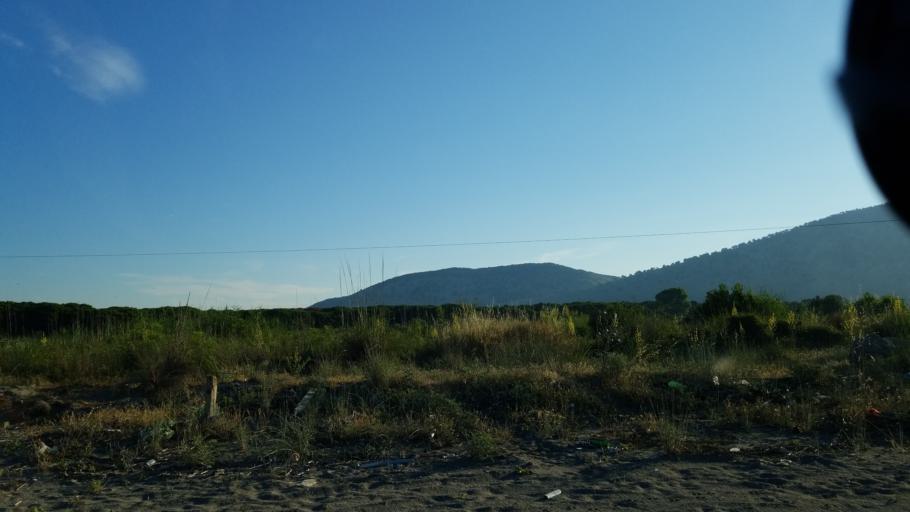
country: AL
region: Shkoder
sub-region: Rrethi i Shkodres
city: Velipoje
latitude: 41.8594
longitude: 19.4429
